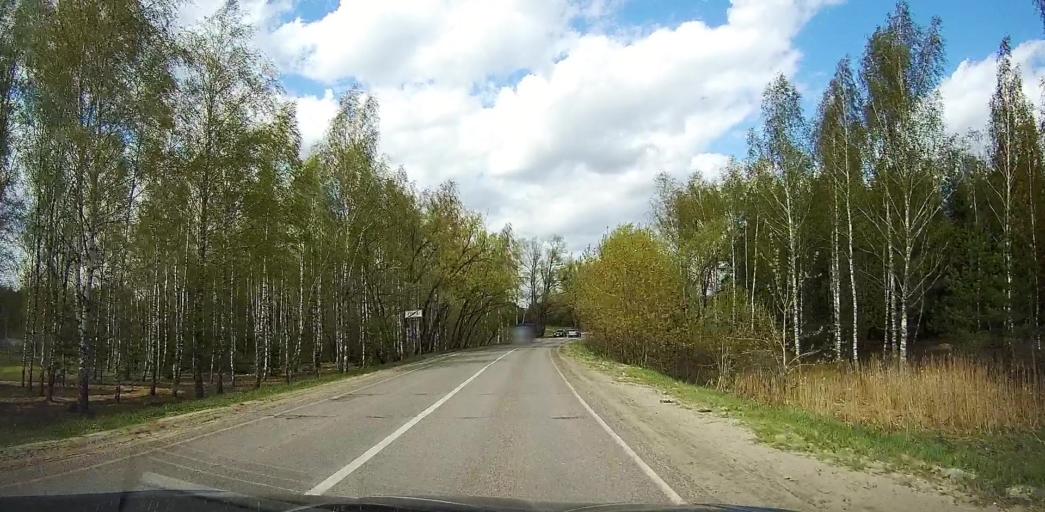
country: RU
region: Moskovskaya
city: Davydovo
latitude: 55.6069
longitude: 38.8477
